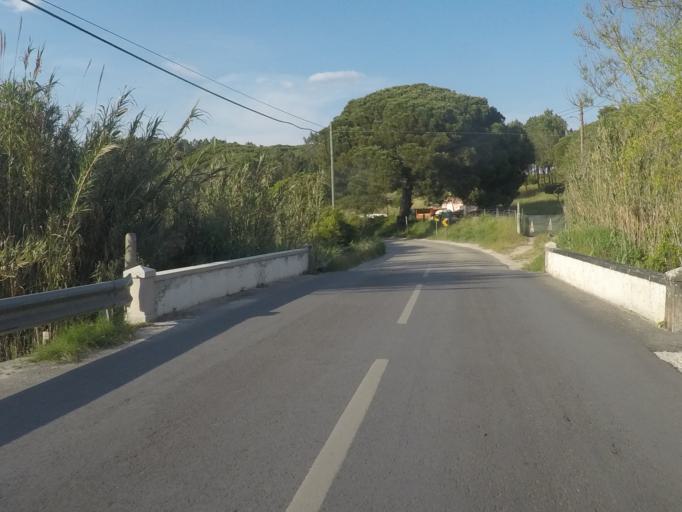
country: PT
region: Setubal
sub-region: Sesimbra
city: Sesimbra
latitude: 38.4731
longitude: -9.1680
